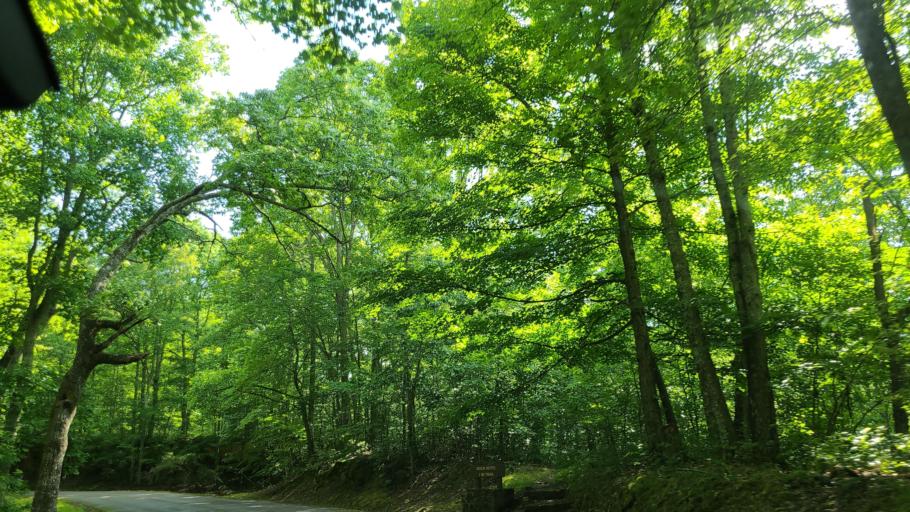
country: US
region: Kentucky
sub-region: Bell County
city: Pineville
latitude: 36.7476
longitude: -83.7121
